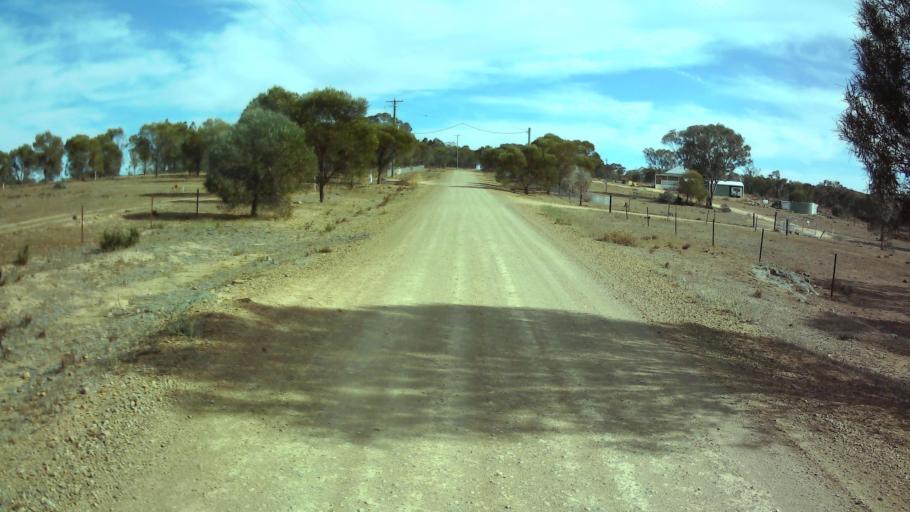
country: AU
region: New South Wales
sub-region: Weddin
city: Grenfell
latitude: -33.8755
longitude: 148.1926
